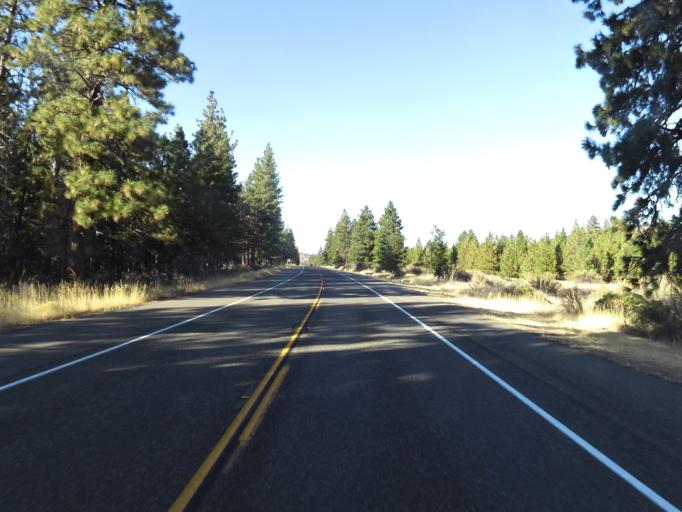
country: US
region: California
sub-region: Siskiyou County
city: Weed
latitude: 41.4573
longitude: -122.3576
